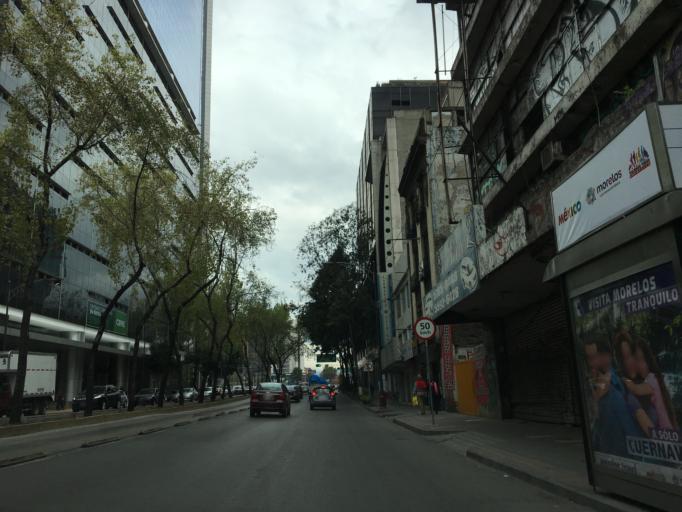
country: MX
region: Mexico City
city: Cuauhtemoc
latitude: 19.4289
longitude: -99.1605
